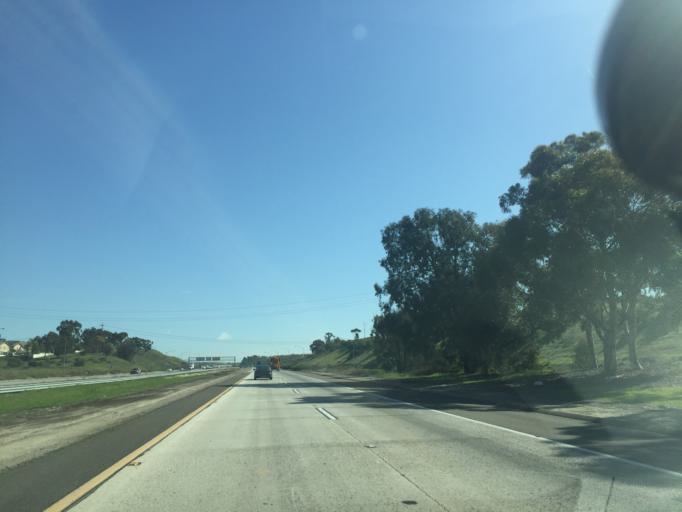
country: MX
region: Baja California
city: Tijuana
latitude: 32.5680
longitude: -117.0366
